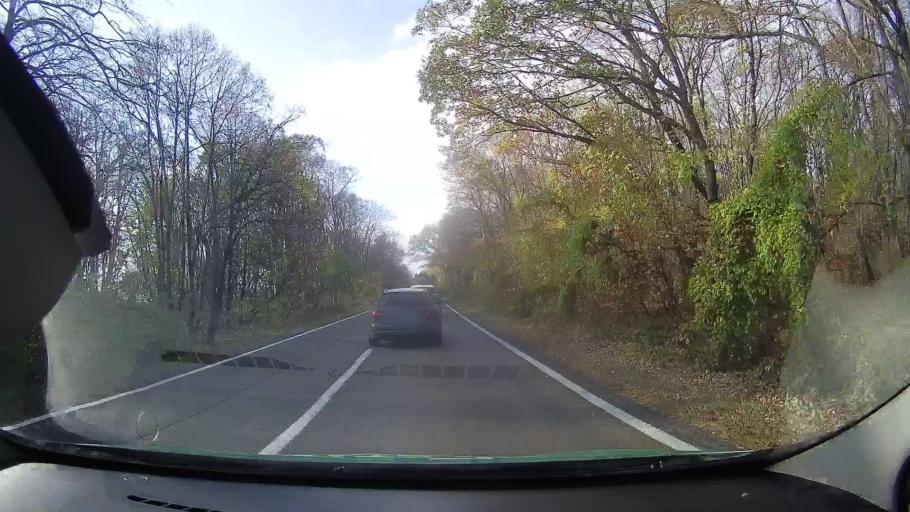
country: RO
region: Tulcea
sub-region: Comuna Topolog
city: Topolog
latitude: 44.9069
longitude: 28.4125
